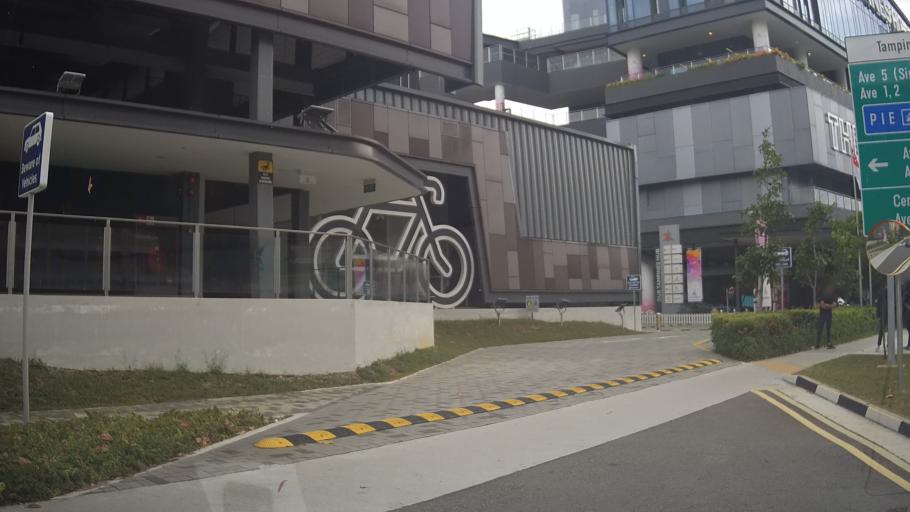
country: SG
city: Singapore
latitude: 1.3518
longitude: 103.9396
